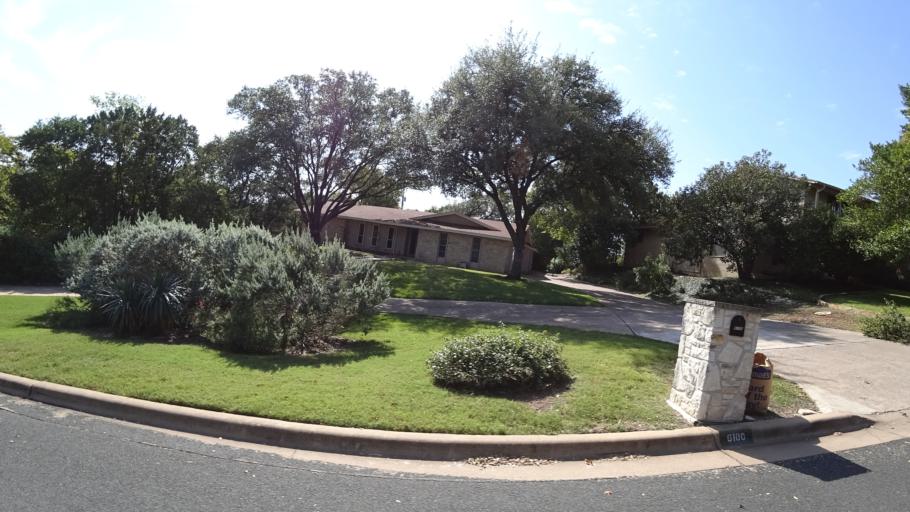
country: US
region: Texas
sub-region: Travis County
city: West Lake Hills
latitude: 30.3484
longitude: -97.7593
